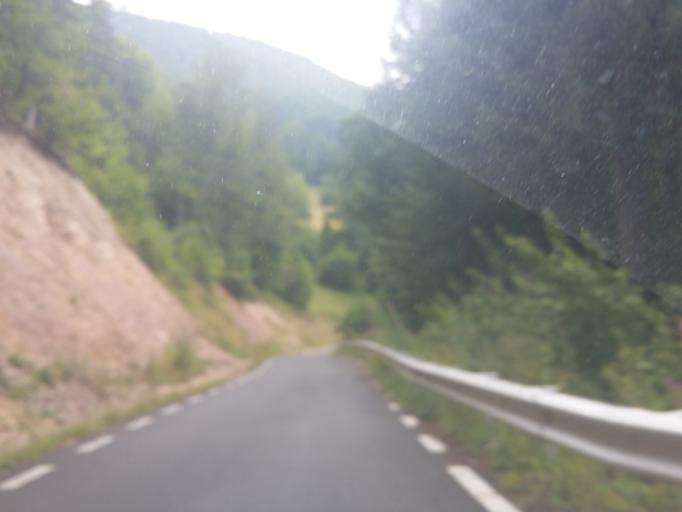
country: RO
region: Alba
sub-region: Comuna Garda de Sus
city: Garda de Sus
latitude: 46.4732
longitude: 22.8153
